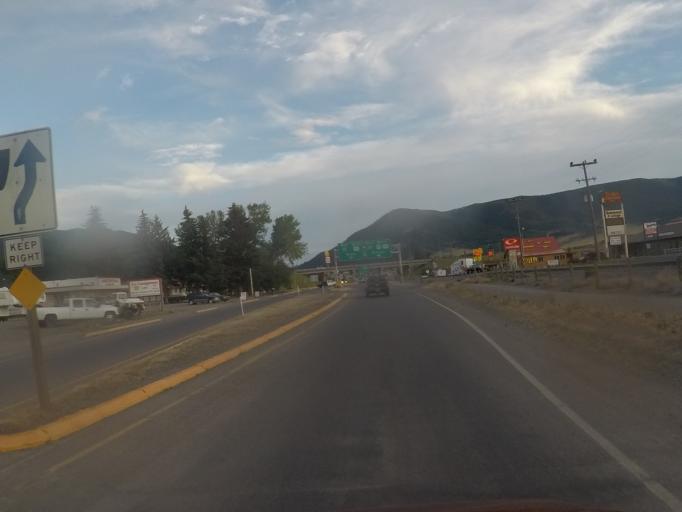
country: US
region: Montana
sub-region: Park County
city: Livingston
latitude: 45.6475
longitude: -110.5730
